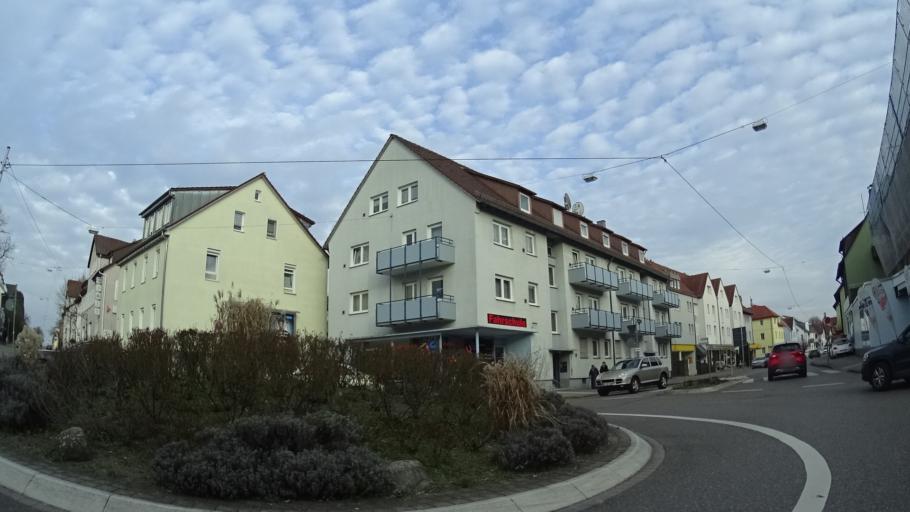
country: DE
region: Baden-Wuerttemberg
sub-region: Regierungsbezirk Stuttgart
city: Leinfelden-Echterdingen
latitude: 48.7271
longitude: 9.1499
